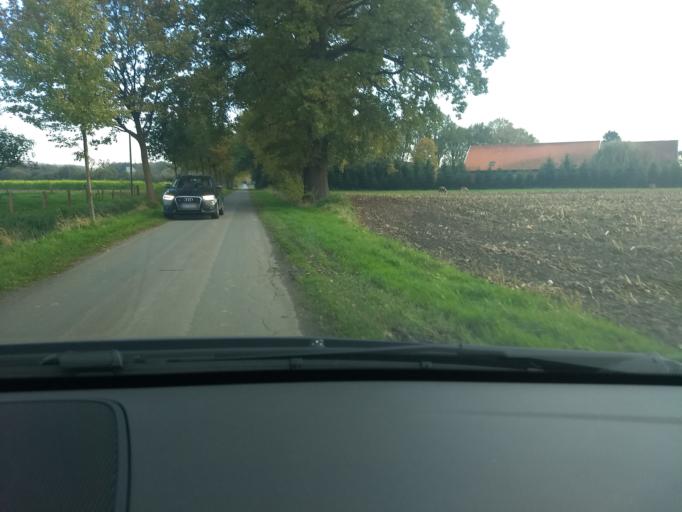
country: DE
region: North Rhine-Westphalia
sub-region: Regierungsbezirk Munster
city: Sudlohn
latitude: 51.8999
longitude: 6.8516
